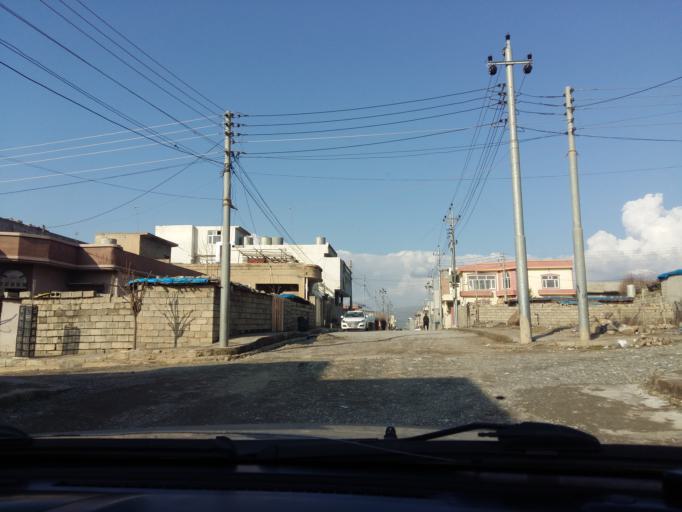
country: IQ
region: As Sulaymaniyah
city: Qeladize
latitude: 36.1760
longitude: 45.1378
